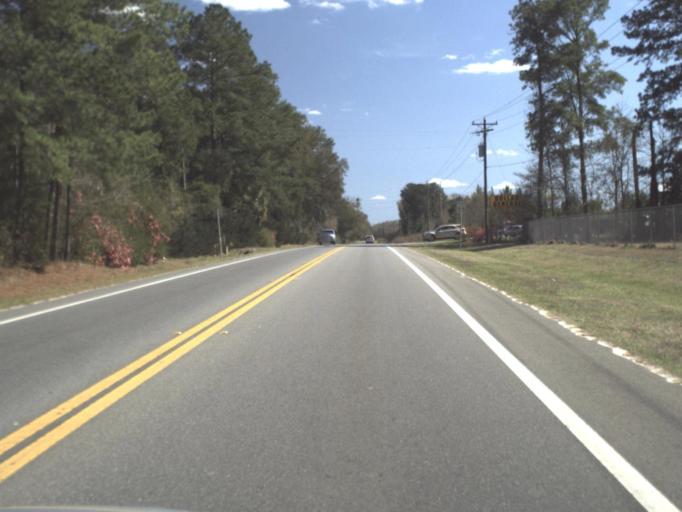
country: US
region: Florida
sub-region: Gadsden County
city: Gretna
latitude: 30.6045
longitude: -84.6544
